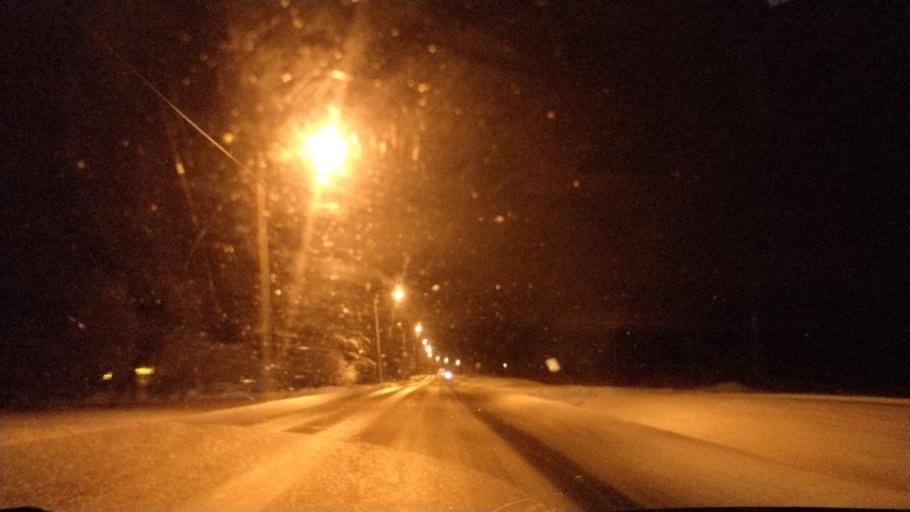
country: FI
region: Lapland
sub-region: Rovaniemi
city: Rovaniemi
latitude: 66.3149
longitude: 25.3619
